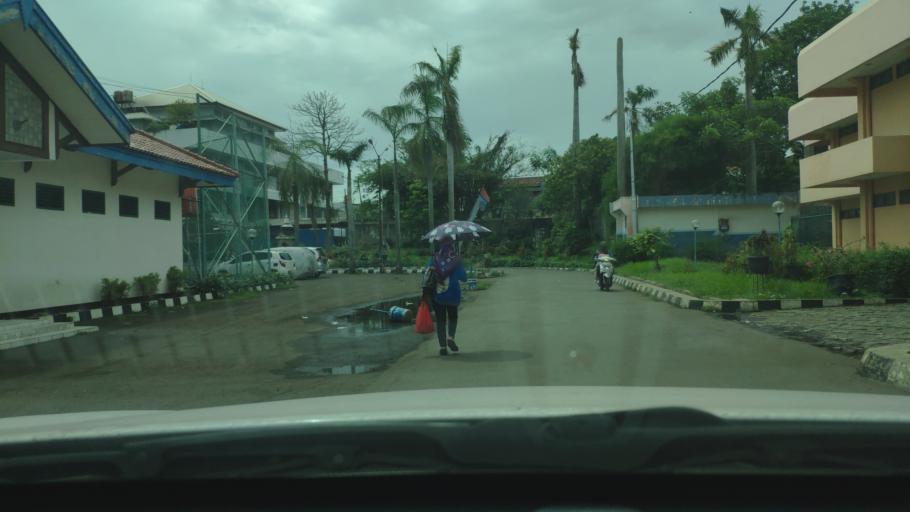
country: ID
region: West Java
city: Ciputat
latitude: -6.2233
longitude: 106.7070
